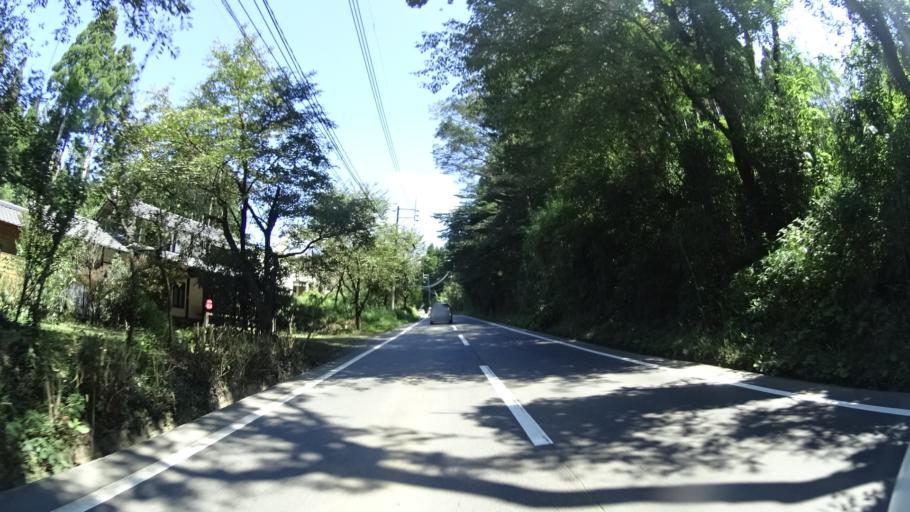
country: JP
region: Kumamoto
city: Aso
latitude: 32.8834
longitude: 130.9984
